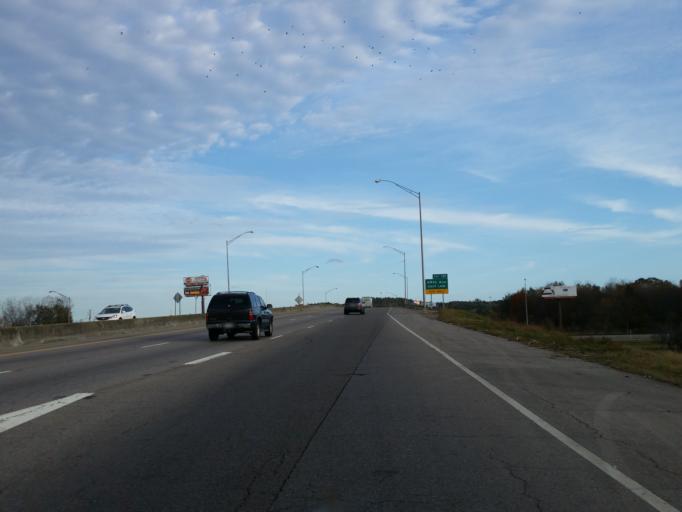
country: US
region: Mississippi
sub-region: Lauderdale County
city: Meridian
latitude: 32.3500
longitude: -88.7370
